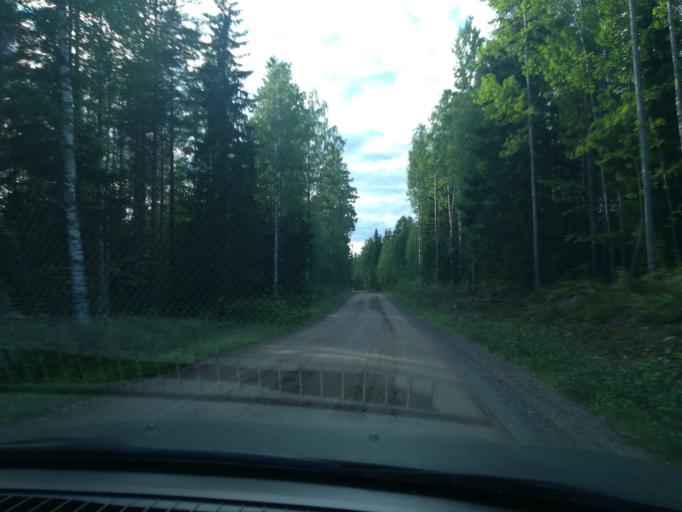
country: FI
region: Southern Savonia
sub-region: Mikkeli
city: Puumala
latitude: 61.5867
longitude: 28.1651
